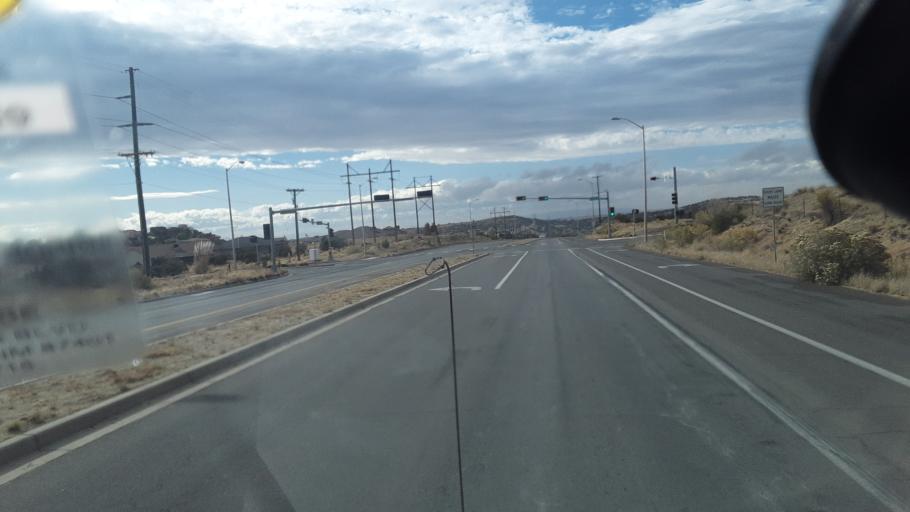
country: US
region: New Mexico
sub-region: San Juan County
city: Farmington
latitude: 36.7737
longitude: -108.1926
